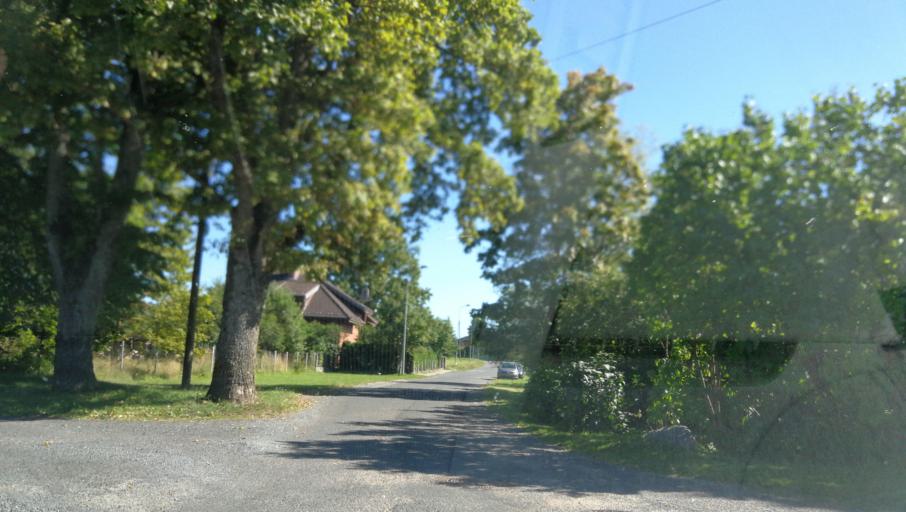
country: LV
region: Cesu Rajons
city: Cesis
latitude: 57.3072
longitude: 25.2468
